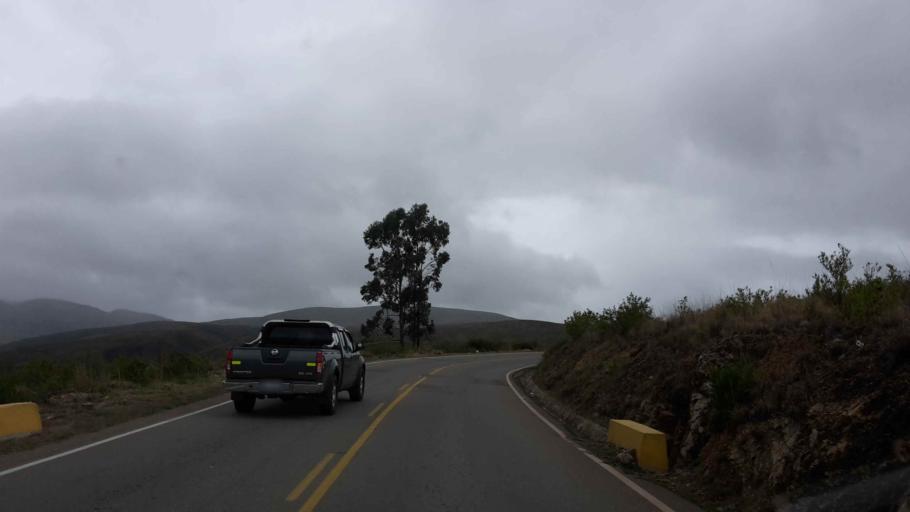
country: BO
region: Cochabamba
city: Arani
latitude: -17.4701
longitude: -65.7660
